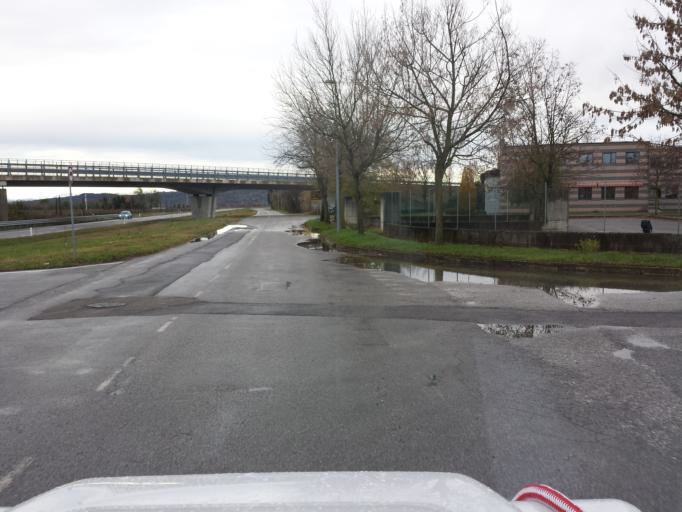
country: IT
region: Friuli Venezia Giulia
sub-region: Provincia di Gorizia
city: Mariano del Friuli
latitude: 45.9028
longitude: 13.4677
